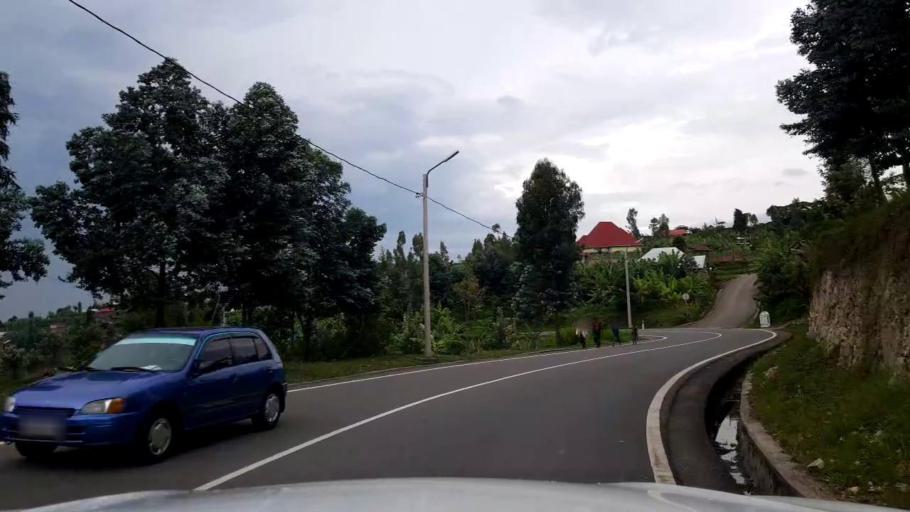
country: RW
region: Western Province
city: Kibuye
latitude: -2.0457
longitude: 29.4086
